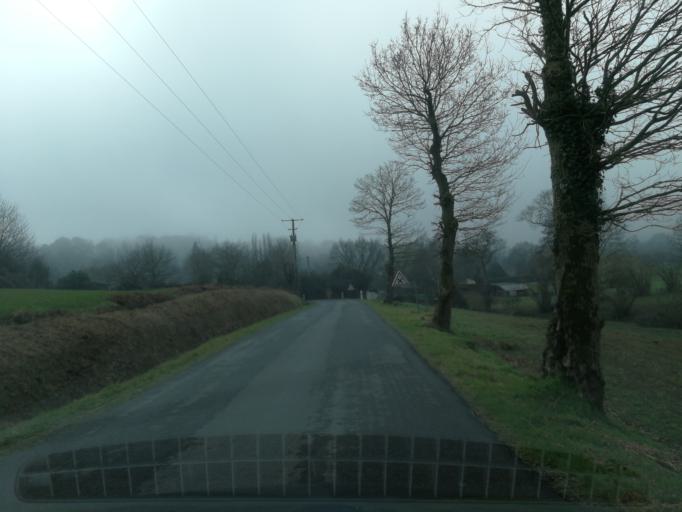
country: FR
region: Brittany
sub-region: Departement du Morbihan
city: La Vraie-Croix
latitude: 47.7340
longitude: -2.5074
